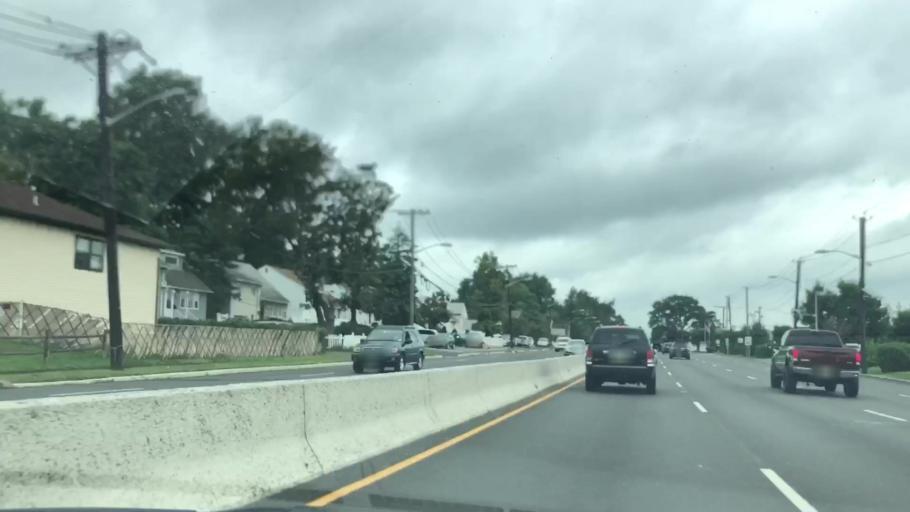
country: US
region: New Jersey
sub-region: Bergen County
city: Elmwood Park
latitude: 40.9059
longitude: -74.1348
